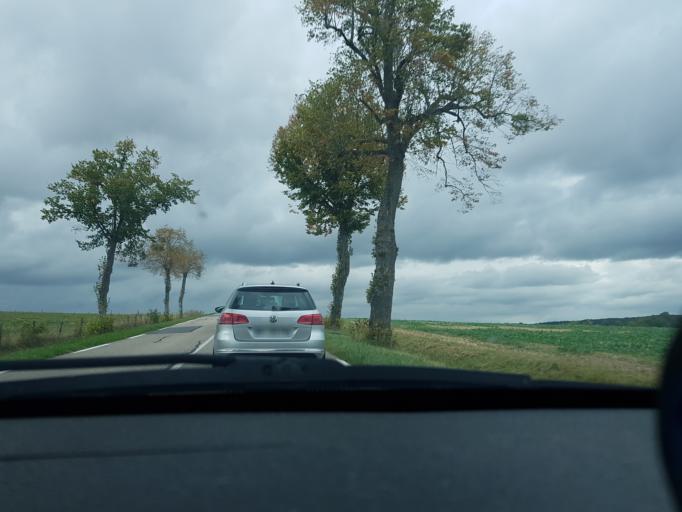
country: FR
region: Lorraine
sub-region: Departement de la Moselle
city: Morhange
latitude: 48.9710
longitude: 6.6098
